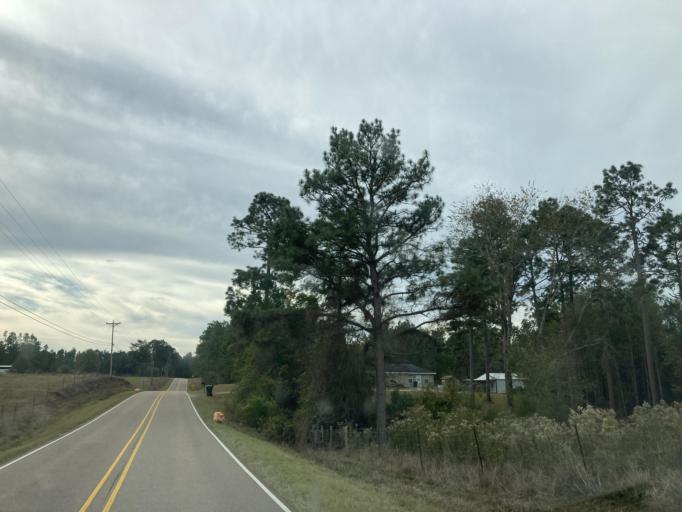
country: US
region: Mississippi
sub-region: Lamar County
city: Purvis
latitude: 31.1018
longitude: -89.4717
